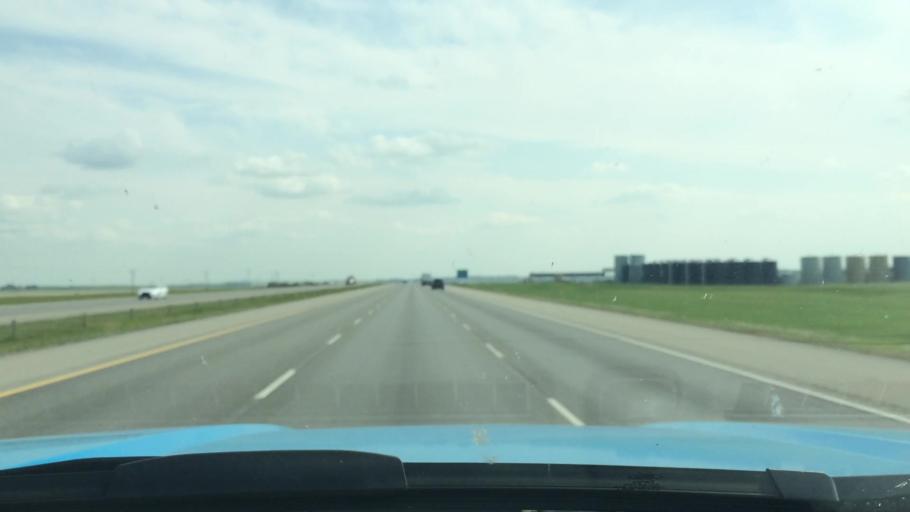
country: CA
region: Alberta
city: Crossfield
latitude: 51.4986
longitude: -114.0254
